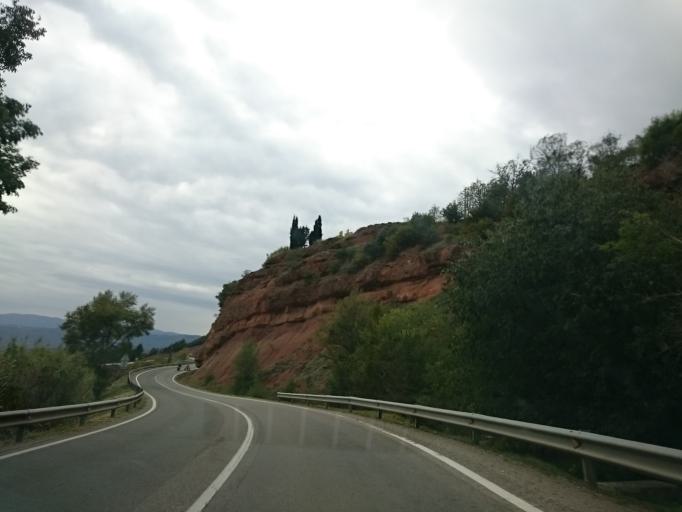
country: ES
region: Catalonia
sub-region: Provincia de Lleida
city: Tremp
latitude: 42.1837
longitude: 0.9005
